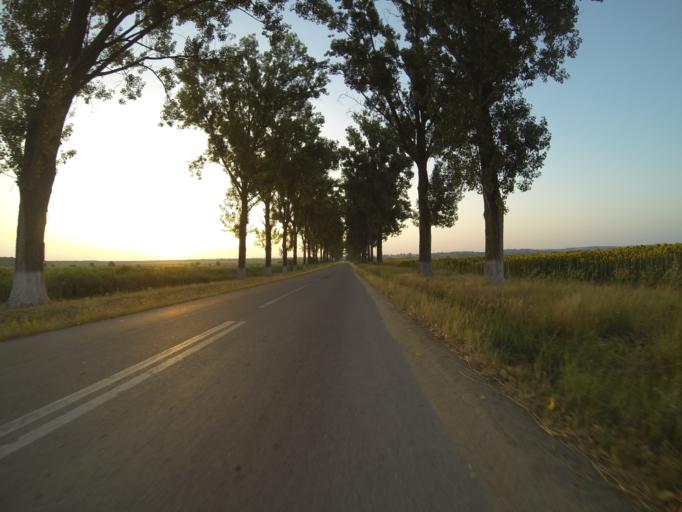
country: RO
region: Dolj
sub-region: Comuna Dobresti
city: Dobresti
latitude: 43.9831
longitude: 23.9206
